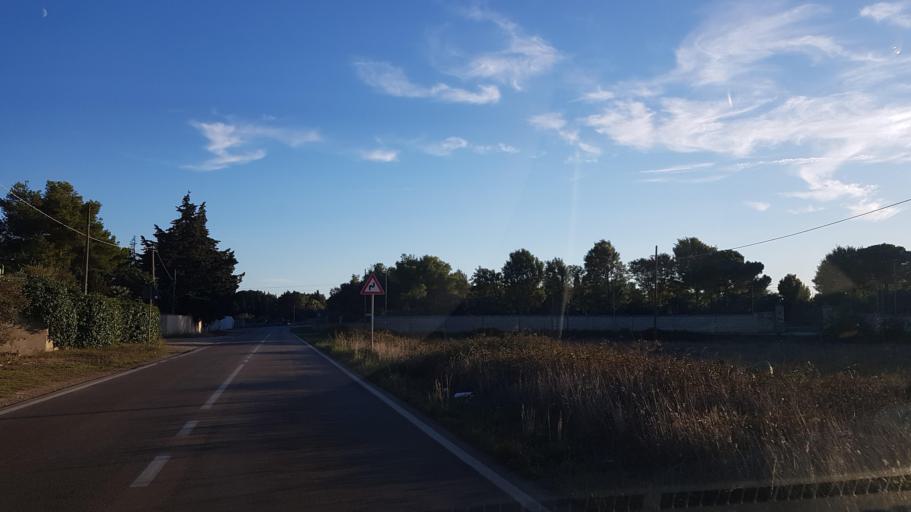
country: IT
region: Apulia
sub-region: Provincia di Lecce
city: Giorgilorio
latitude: 40.3961
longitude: 18.1944
